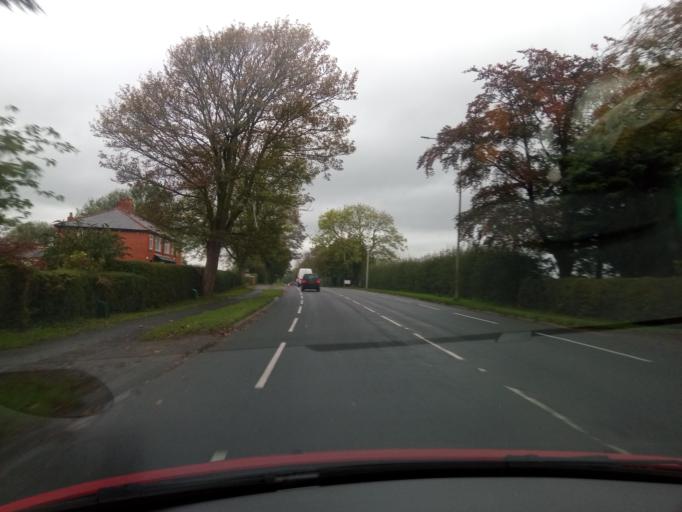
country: GB
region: England
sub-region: Lancashire
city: Catterall
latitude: 53.8467
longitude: -2.7441
